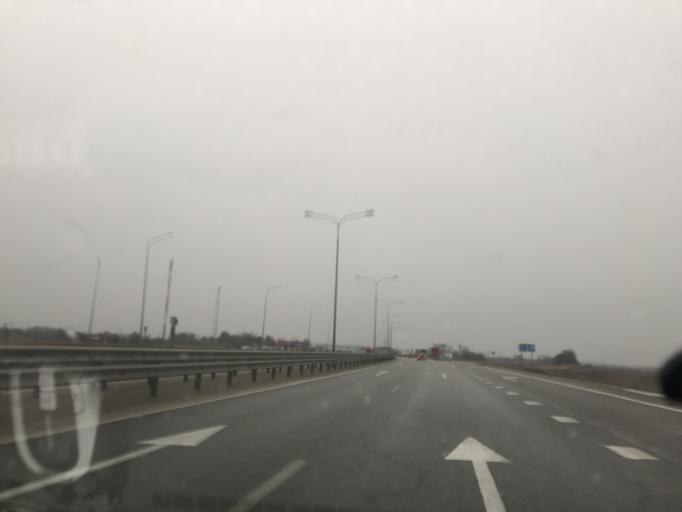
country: RU
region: Krasnodarskiy
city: Krylovskaya
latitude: 46.2800
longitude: 39.8310
